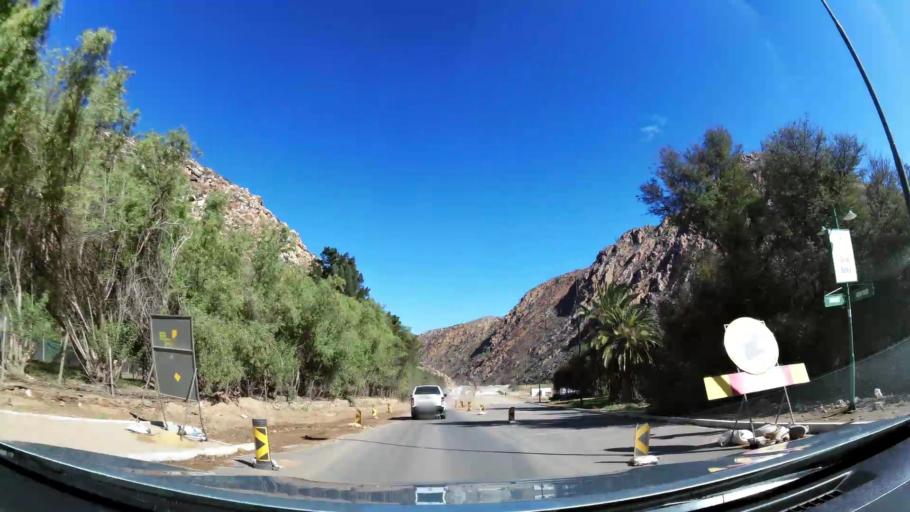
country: ZA
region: Western Cape
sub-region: Cape Winelands District Municipality
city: Ashton
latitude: -33.7928
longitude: 20.1075
